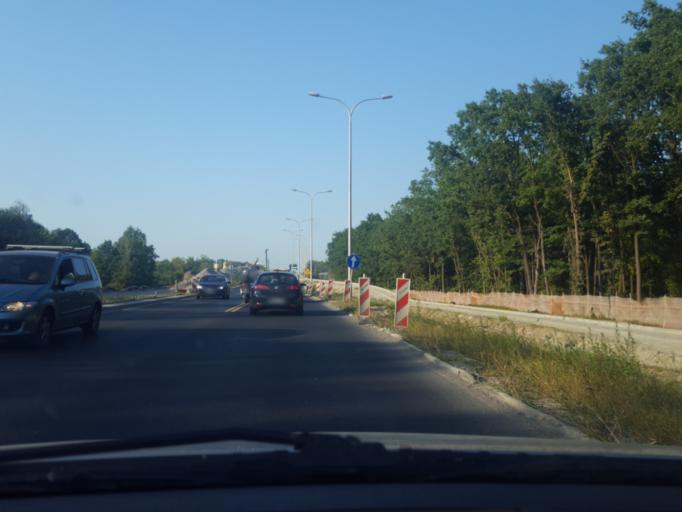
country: PL
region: Masovian Voivodeship
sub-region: Warszawa
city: Rembertow
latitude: 52.2544
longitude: 21.1406
